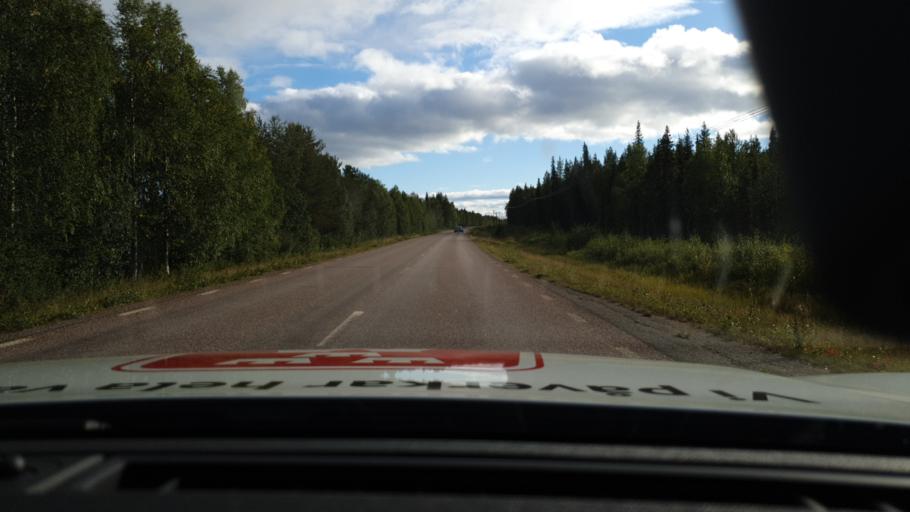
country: SE
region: Norrbotten
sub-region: Pajala Kommun
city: Pajala
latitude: 67.1187
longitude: 22.6049
